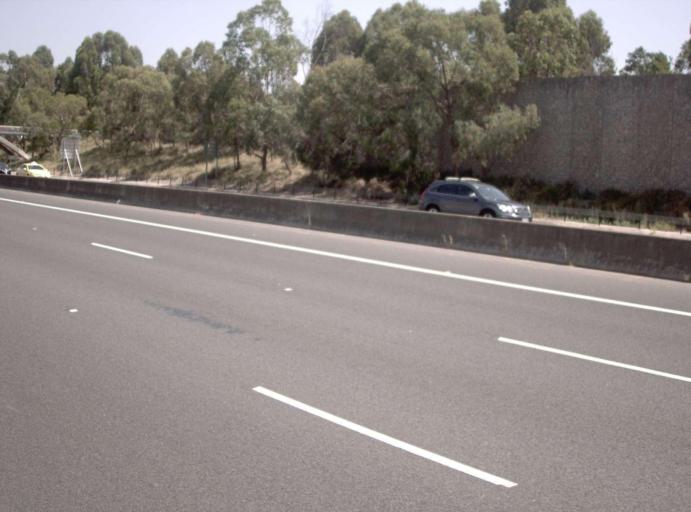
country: AU
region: Victoria
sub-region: Whitehorse
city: Blackburn North
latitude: -37.8007
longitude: 145.1532
